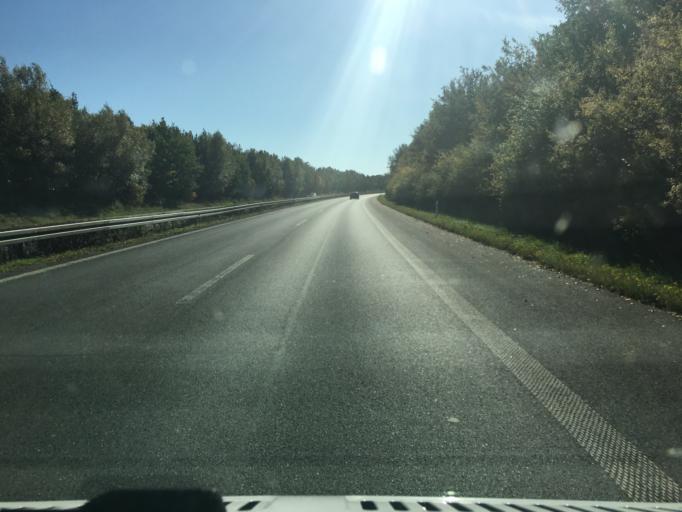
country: DE
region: Saxony
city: Dennheritz
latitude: 50.8064
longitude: 12.4543
